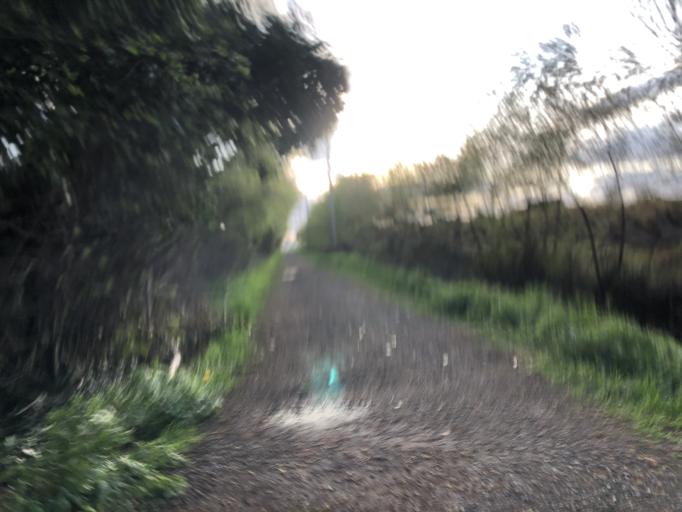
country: CA
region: British Columbia
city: Richmond
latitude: 49.1480
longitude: -123.1092
